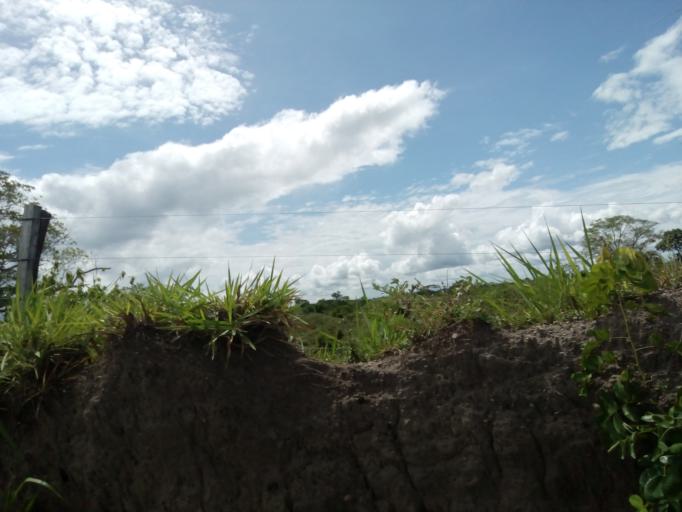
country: CO
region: Boyaca
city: Puerto Boyaca
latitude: 5.9901
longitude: -74.4084
